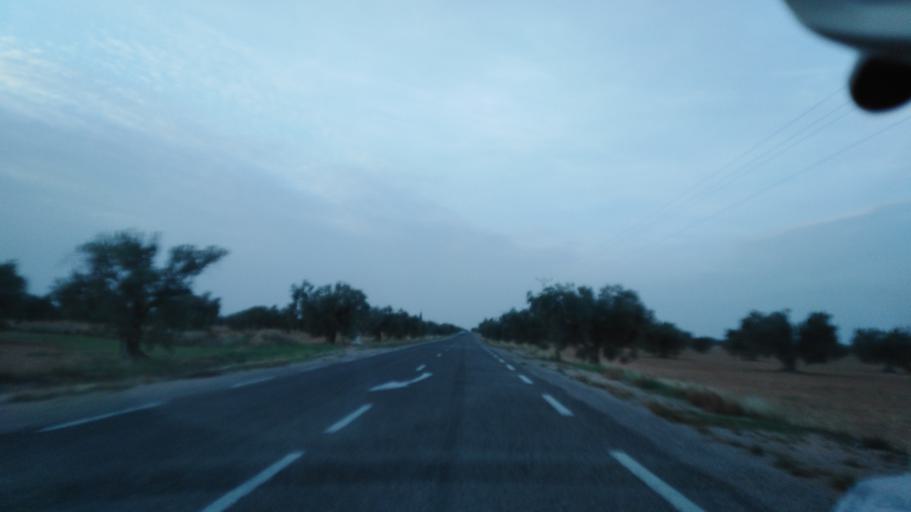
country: TN
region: Safaqis
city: Bi'r `Ali Bin Khalifah
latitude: 34.9051
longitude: 10.3879
